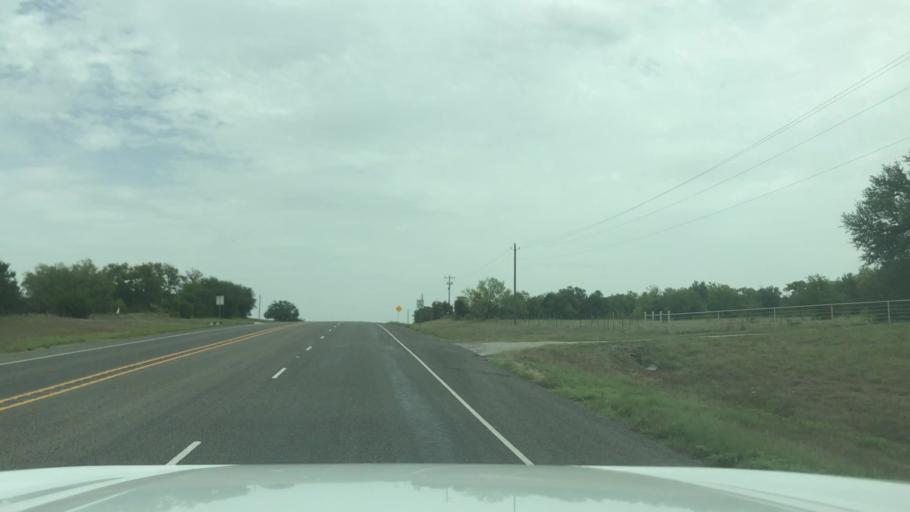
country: US
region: Texas
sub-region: Hamilton County
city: Hico
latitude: 31.9807
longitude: -98.0182
